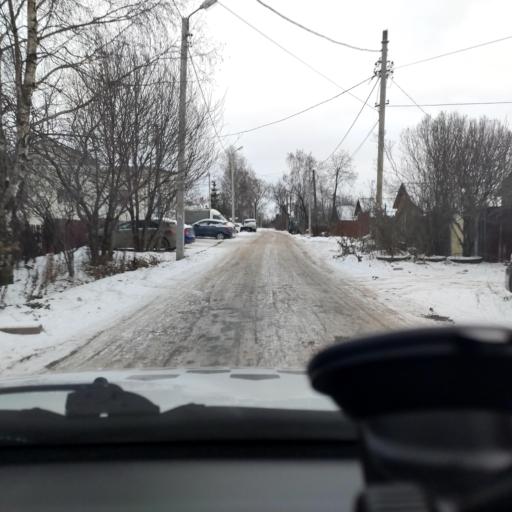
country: RU
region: Perm
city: Froly
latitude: 57.9562
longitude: 56.2875
